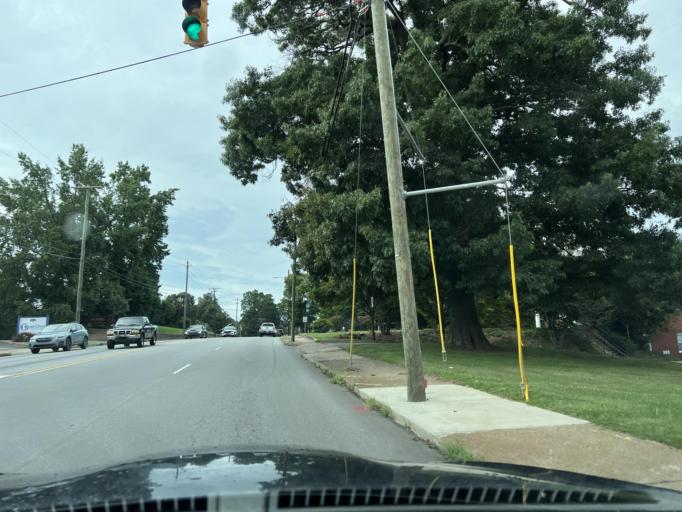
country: US
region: North Carolina
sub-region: Buncombe County
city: Asheville
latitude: 35.5802
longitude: -82.6081
